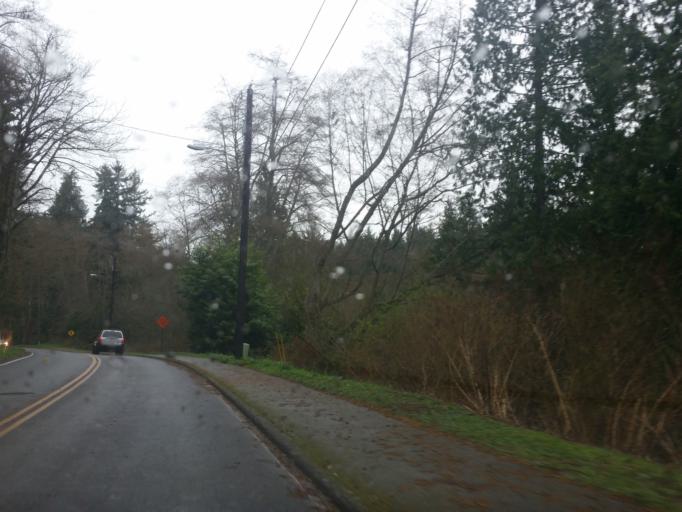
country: US
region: Washington
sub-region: Snohomish County
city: Meadowdale
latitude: 47.8342
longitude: -122.3390
